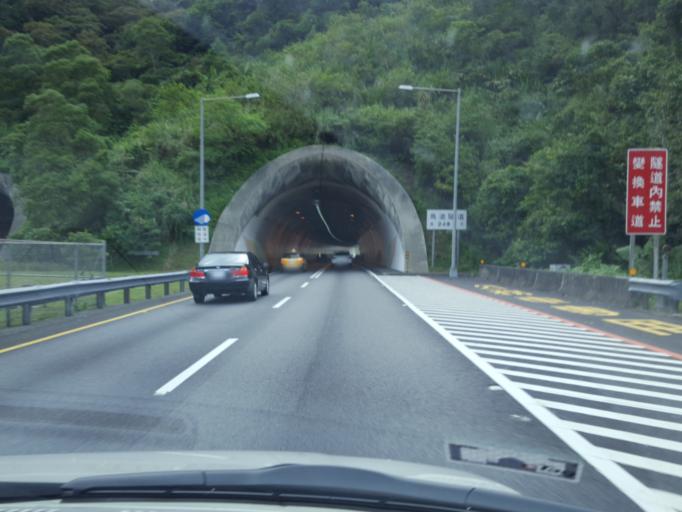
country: TW
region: Taipei
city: Taipei
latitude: 24.9823
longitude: 121.6676
